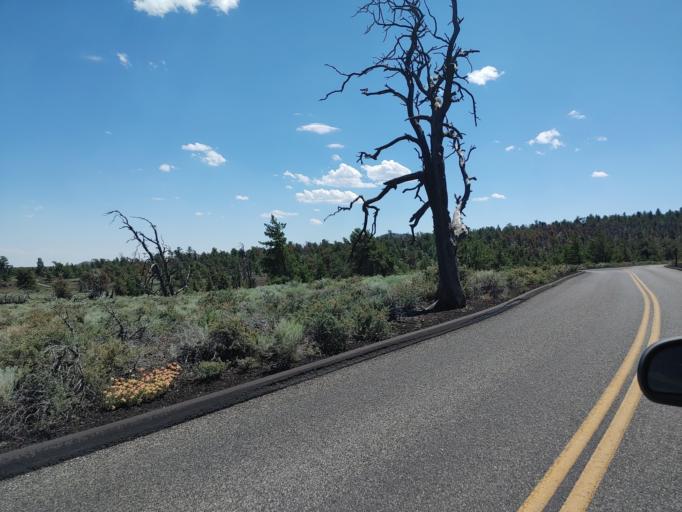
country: US
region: Idaho
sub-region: Butte County
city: Arco
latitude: 43.4505
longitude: -113.5432
